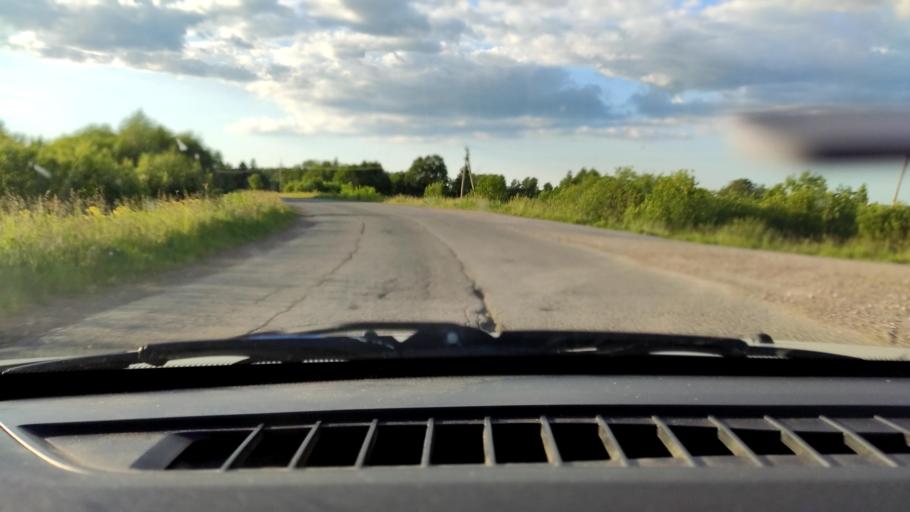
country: RU
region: Perm
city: Uinskoye
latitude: 57.0865
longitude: 56.5587
